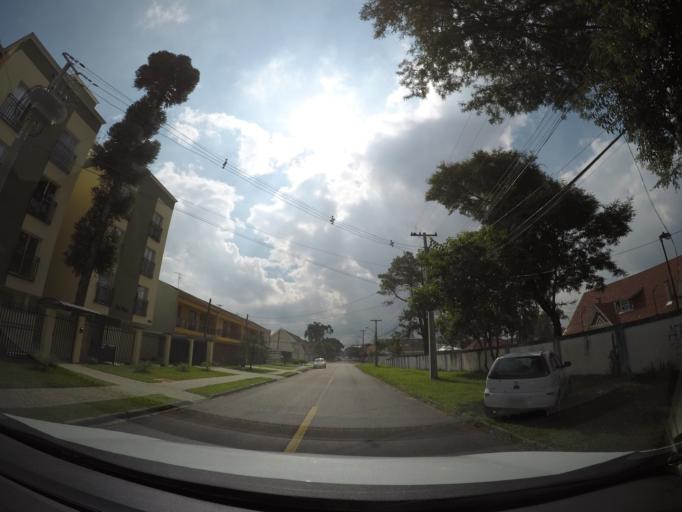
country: BR
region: Parana
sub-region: Curitiba
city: Curitiba
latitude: -25.4807
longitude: -49.2517
